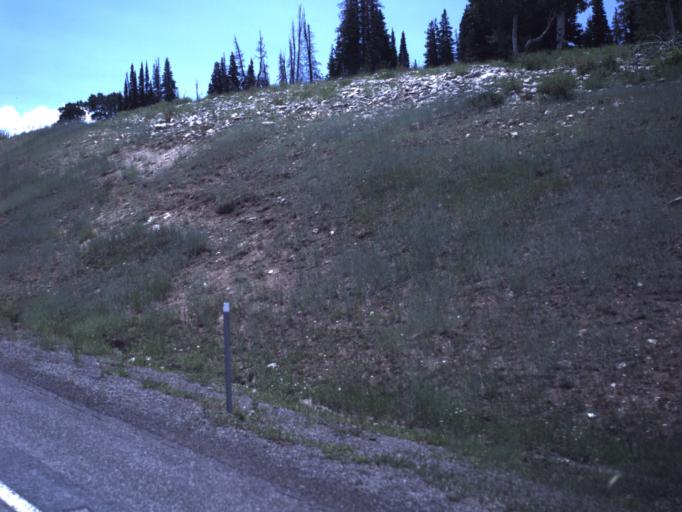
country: US
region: Utah
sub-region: Sanpete County
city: Fairview
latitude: 39.6427
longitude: -111.3304
